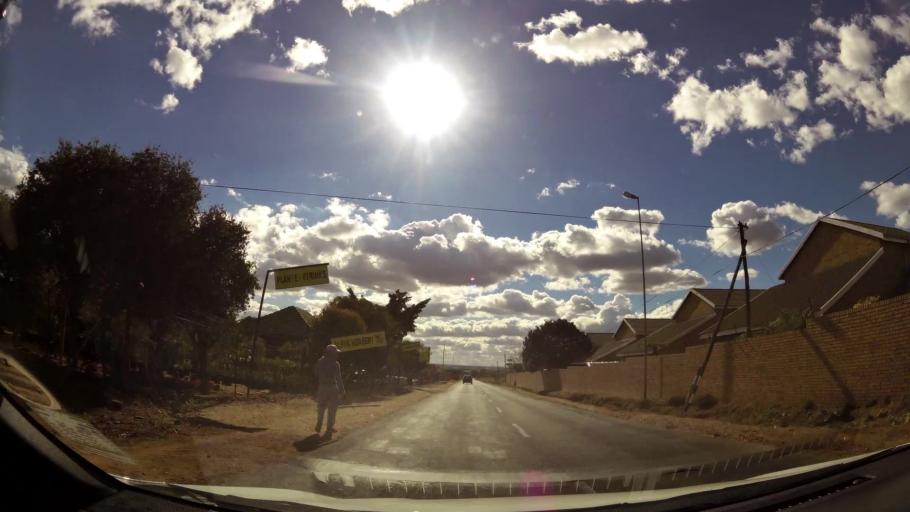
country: ZA
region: Limpopo
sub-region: Capricorn District Municipality
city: Polokwane
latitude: -23.8805
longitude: 29.4824
